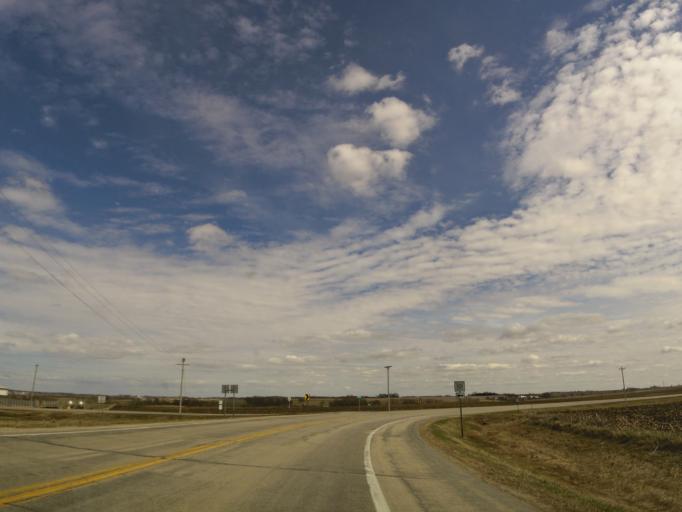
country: US
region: Minnesota
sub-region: Olmsted County
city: Rochester
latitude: 43.9566
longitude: -92.4196
